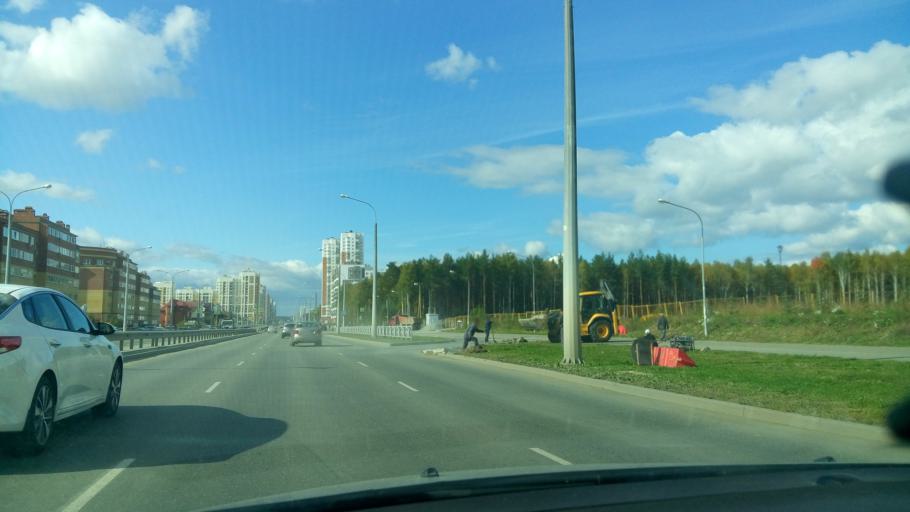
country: RU
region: Sverdlovsk
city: Sovkhoznyy
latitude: 56.7834
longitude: 60.5391
